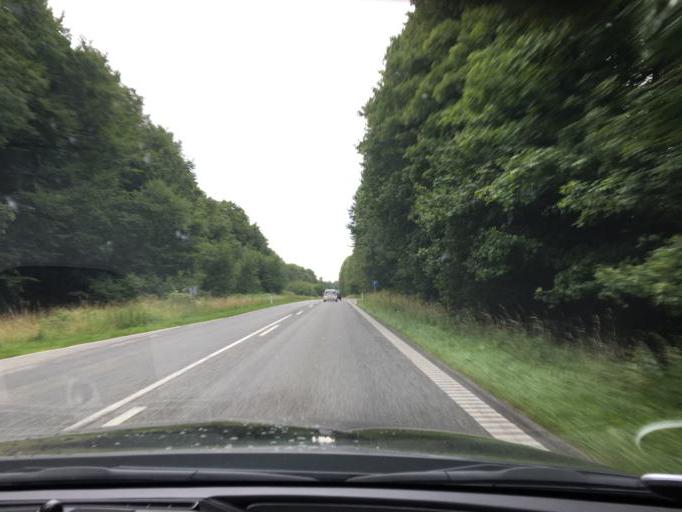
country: DK
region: Capital Region
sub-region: Allerod Kommune
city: Blovstrod
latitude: 55.9140
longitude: 12.3905
